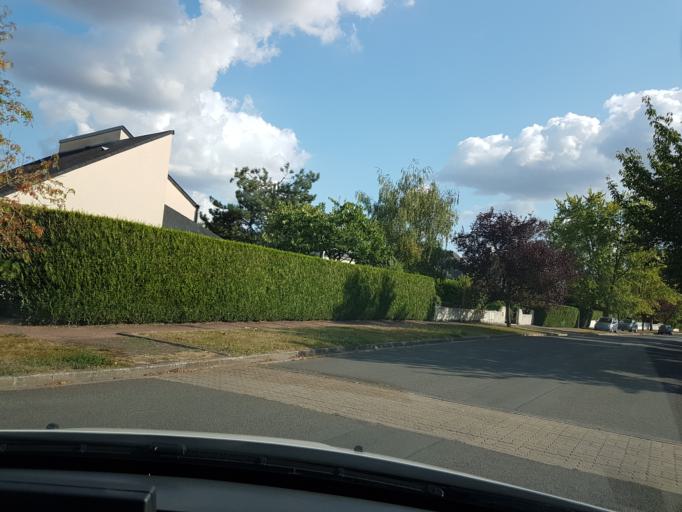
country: FR
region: Centre
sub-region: Departement d'Indre-et-Loire
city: Saint-Avertin
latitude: 47.3646
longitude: 0.7523
